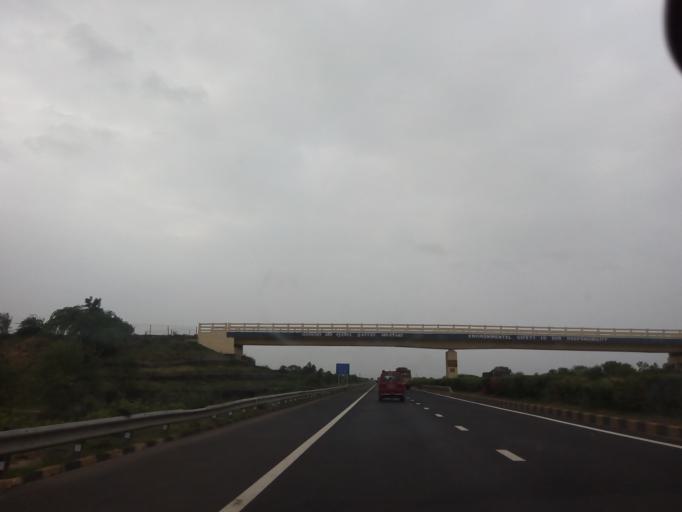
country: IN
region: Gujarat
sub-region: Kheda
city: Mahemdavad
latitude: 22.8079
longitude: 72.8357
